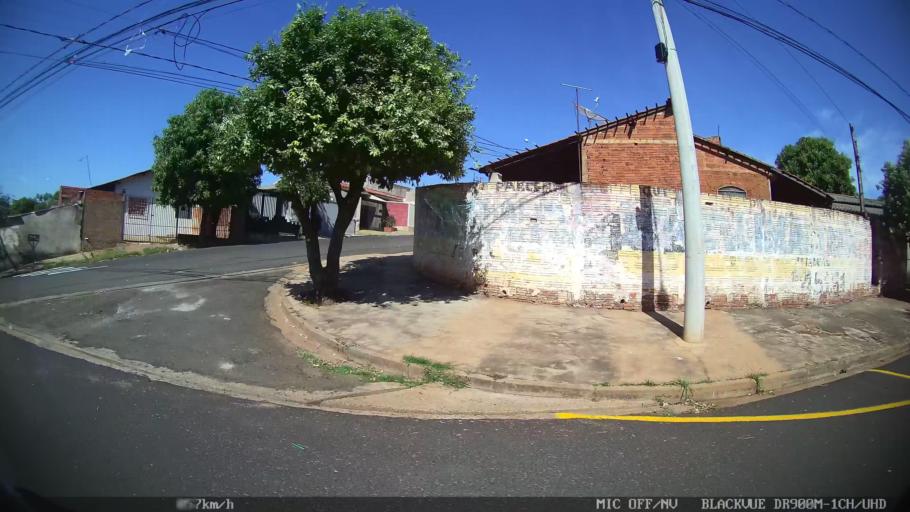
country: BR
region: Sao Paulo
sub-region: Sao Jose Do Rio Preto
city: Sao Jose do Rio Preto
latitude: -20.7741
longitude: -49.4096
